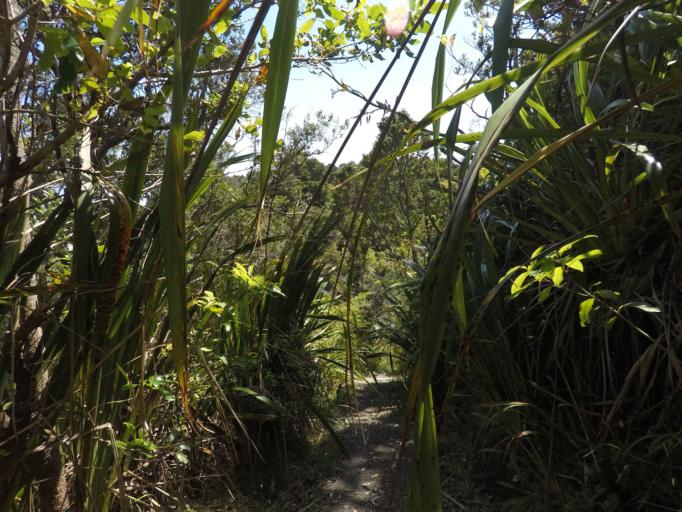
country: NZ
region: Auckland
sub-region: Auckland
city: Titirangi
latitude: -36.9774
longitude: 174.6308
